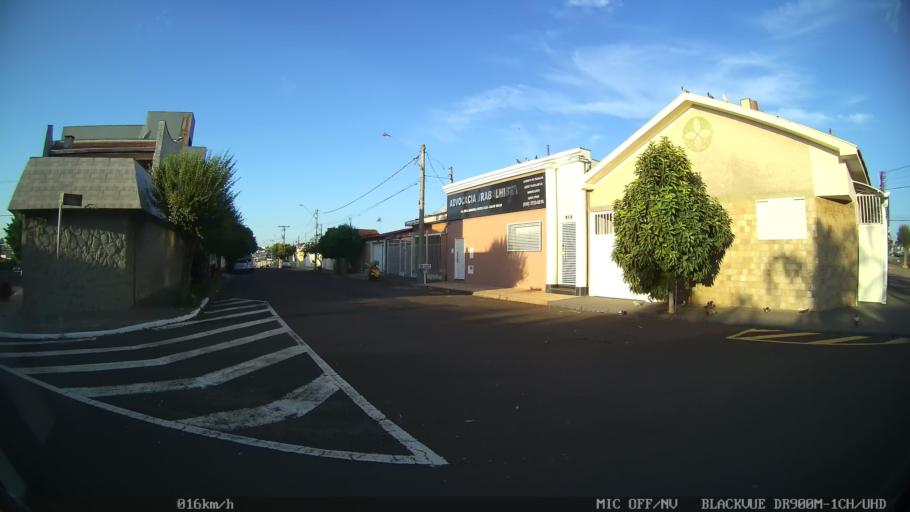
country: BR
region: Sao Paulo
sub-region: Franca
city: Franca
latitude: -20.5242
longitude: -47.3951
